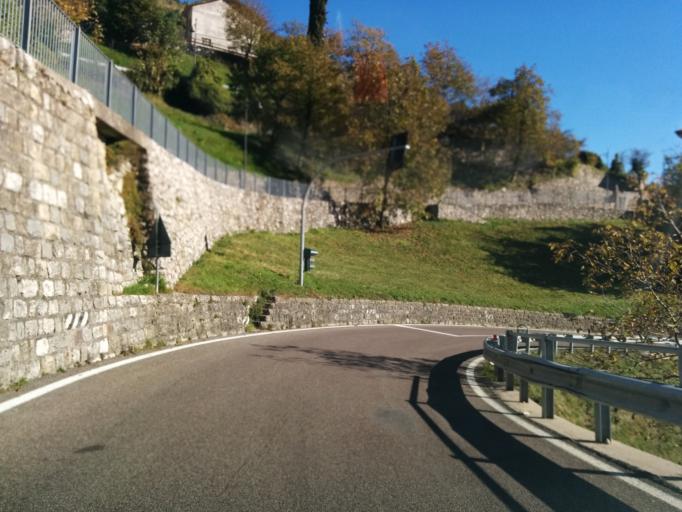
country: IT
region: Trentino-Alto Adige
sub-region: Provincia di Trento
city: Tenno
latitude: 45.9291
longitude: 10.8243
